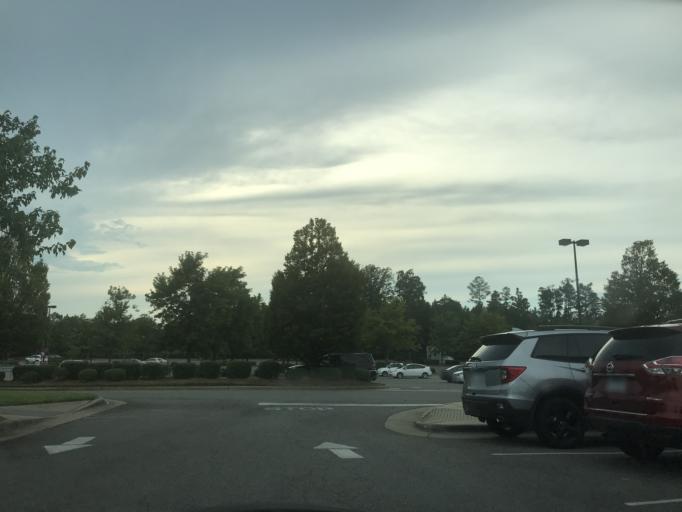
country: US
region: North Carolina
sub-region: Wake County
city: Morrisville
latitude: 35.9037
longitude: -78.7846
